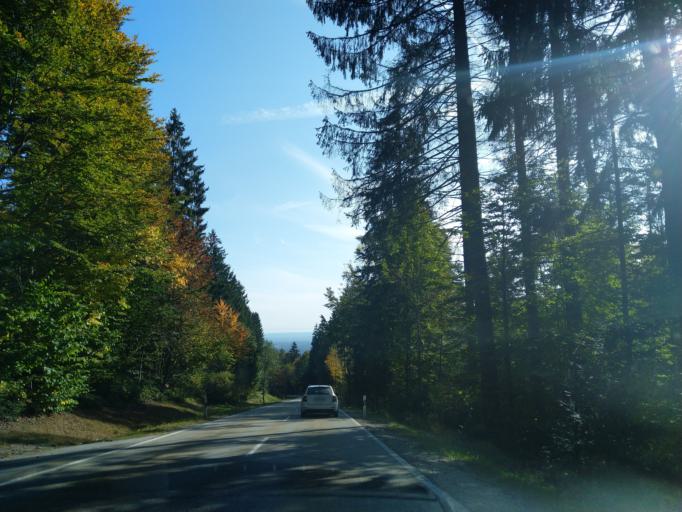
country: DE
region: Bavaria
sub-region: Lower Bavaria
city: Achslach
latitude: 48.9360
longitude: 12.9259
